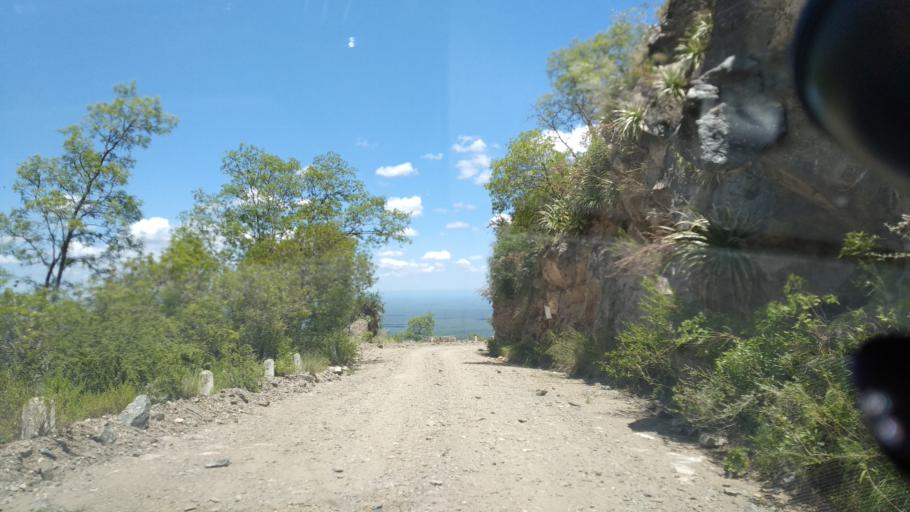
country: AR
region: Cordoba
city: Salsacate
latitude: -31.3706
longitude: -65.4068
